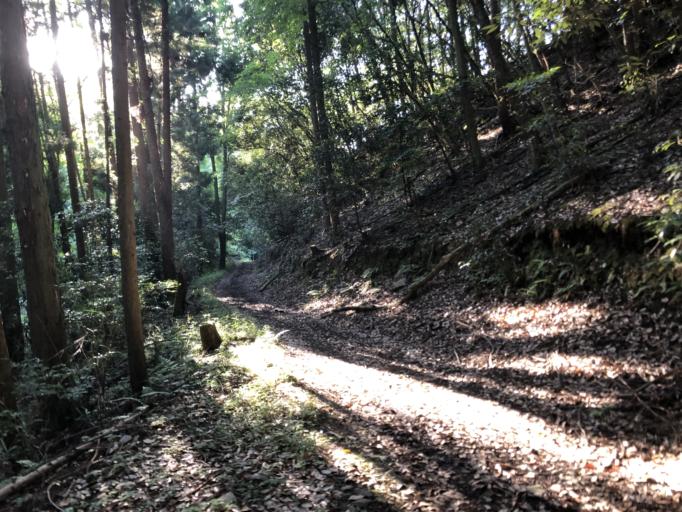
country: JP
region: Kyoto
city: Kameoka
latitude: 34.9889
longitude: 135.6226
